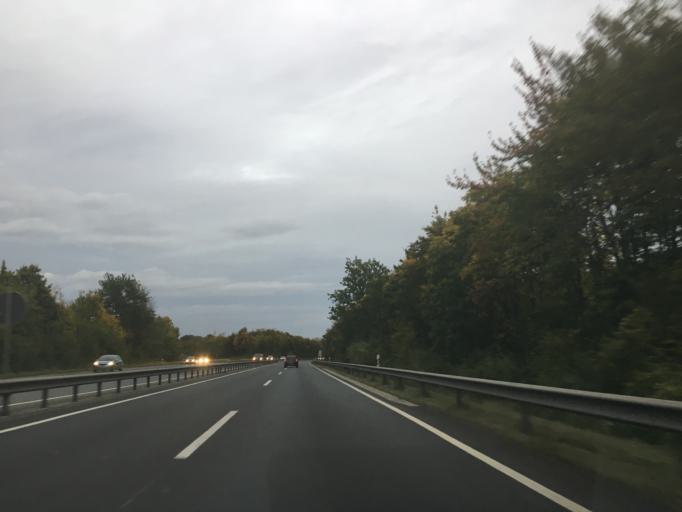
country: DE
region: Rheinland-Pfalz
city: Budenheim
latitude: 49.9998
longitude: 8.1760
